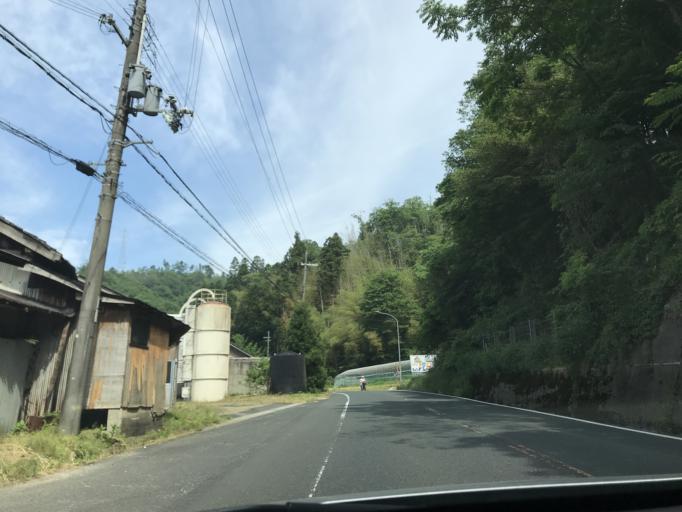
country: JP
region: Kyoto
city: Miyazu
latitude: 35.6626
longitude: 135.0164
